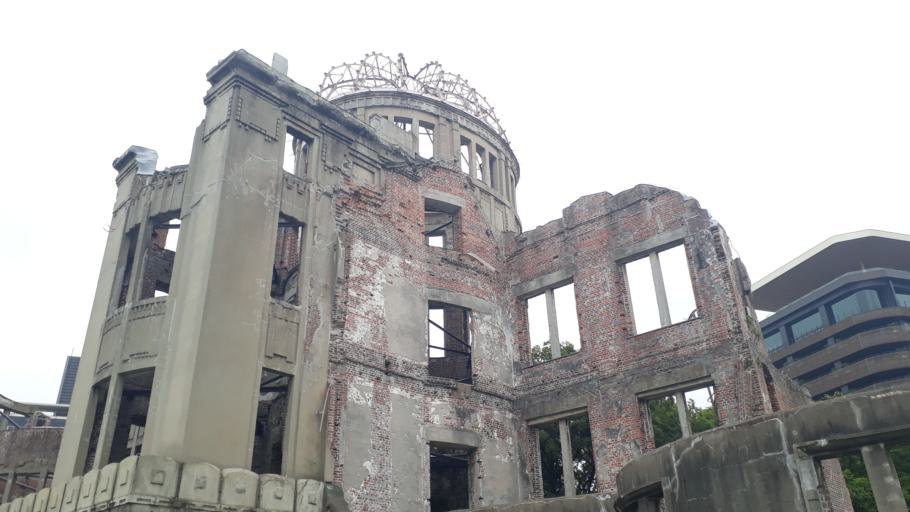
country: JP
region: Hiroshima
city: Hiroshima-shi
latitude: 34.3953
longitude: 132.4533
